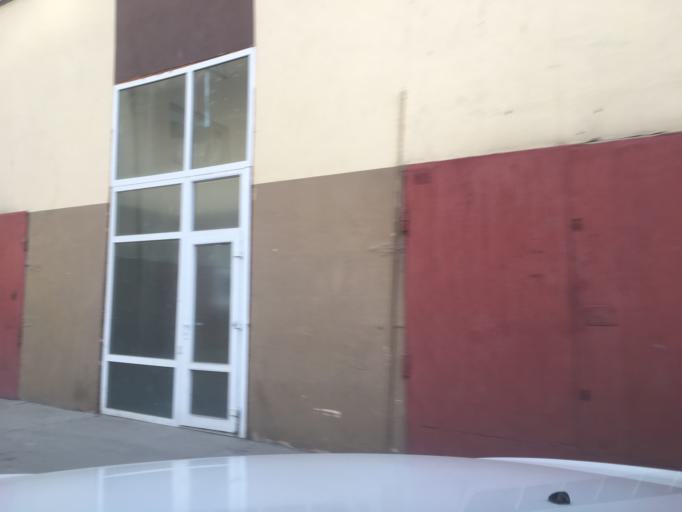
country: MN
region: Ulaanbaatar
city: Ulaanbaatar
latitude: 47.9172
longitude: 106.8722
